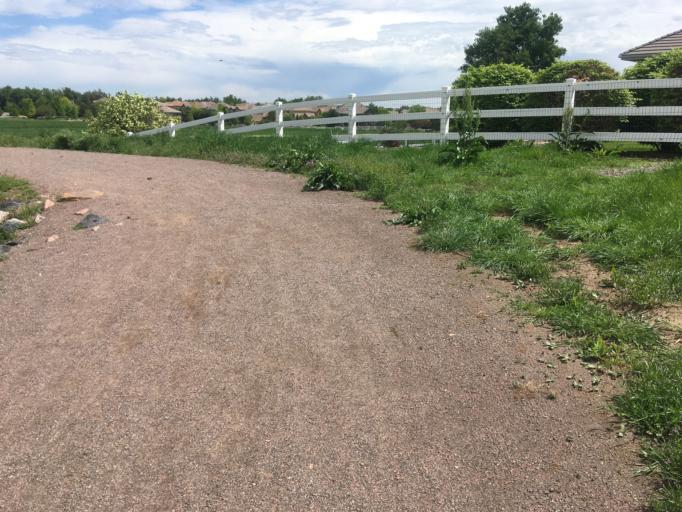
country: US
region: Colorado
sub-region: Adams County
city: Northglenn
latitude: 39.9538
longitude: -105.0072
